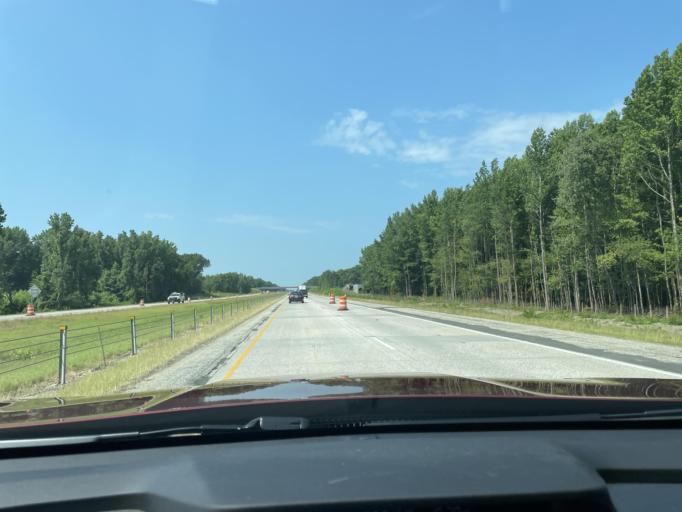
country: US
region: Arkansas
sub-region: White County
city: Searcy
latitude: 35.1763
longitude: -91.7637
